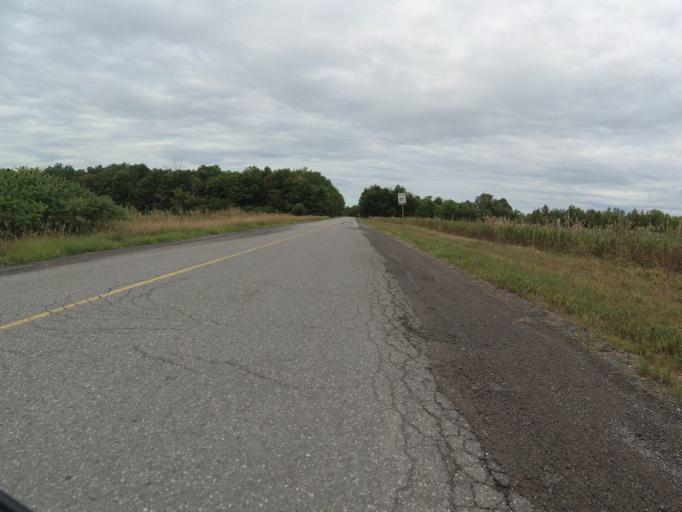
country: CA
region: Ontario
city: Clarence-Rockland
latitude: 45.4315
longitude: -75.3004
